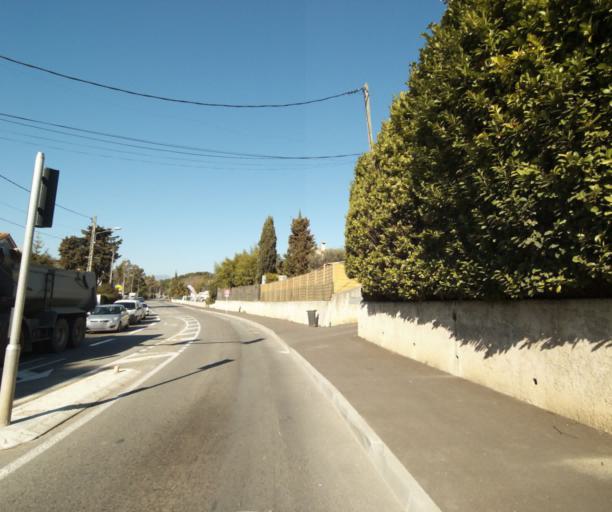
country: FR
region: Provence-Alpes-Cote d'Azur
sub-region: Departement des Alpes-Maritimes
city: Biot
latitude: 43.5974
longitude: 7.1047
